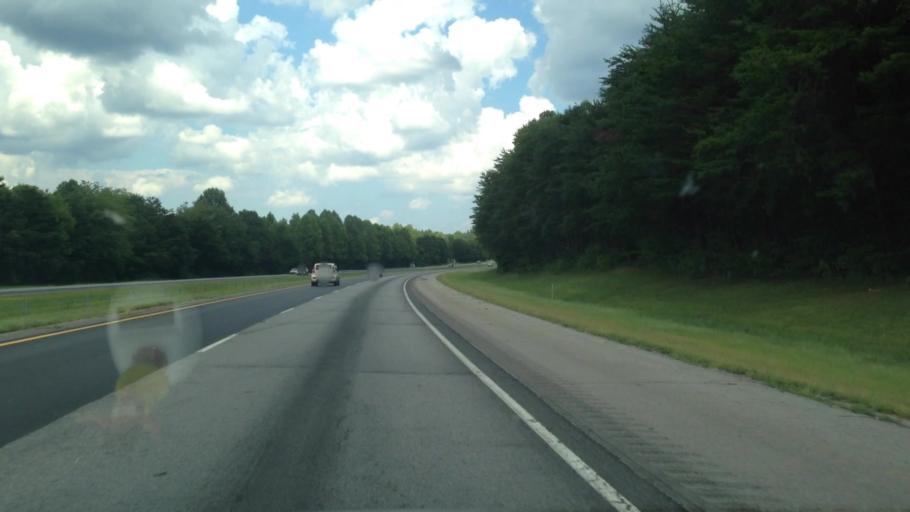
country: US
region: Virginia
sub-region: City of Danville
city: Danville
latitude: 36.4695
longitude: -79.5245
